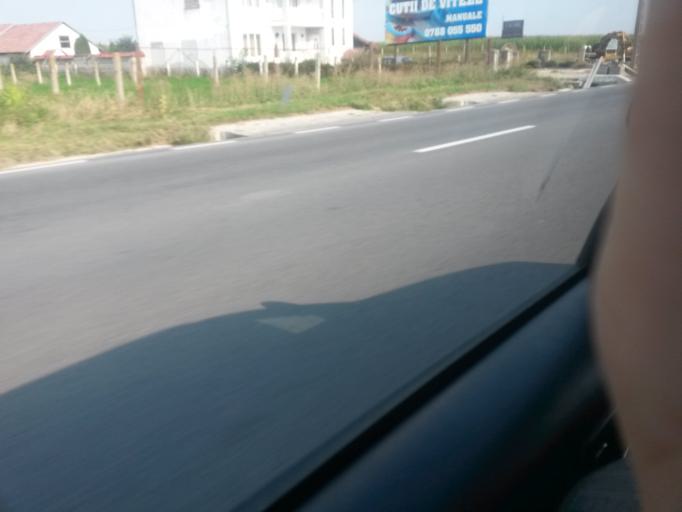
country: RO
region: Cluj
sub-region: Comuna Sandulesti
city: Copaceni
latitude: 46.5982
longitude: 23.7436
